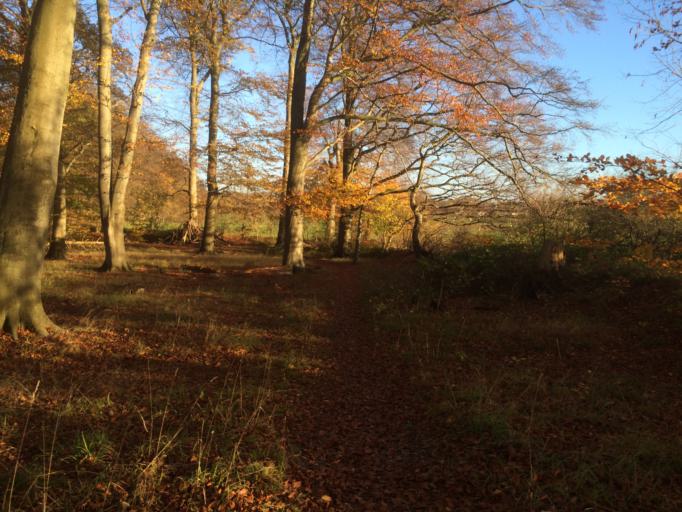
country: DK
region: Capital Region
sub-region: Fureso Kommune
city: Vaerlose
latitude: 55.7893
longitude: 12.3506
